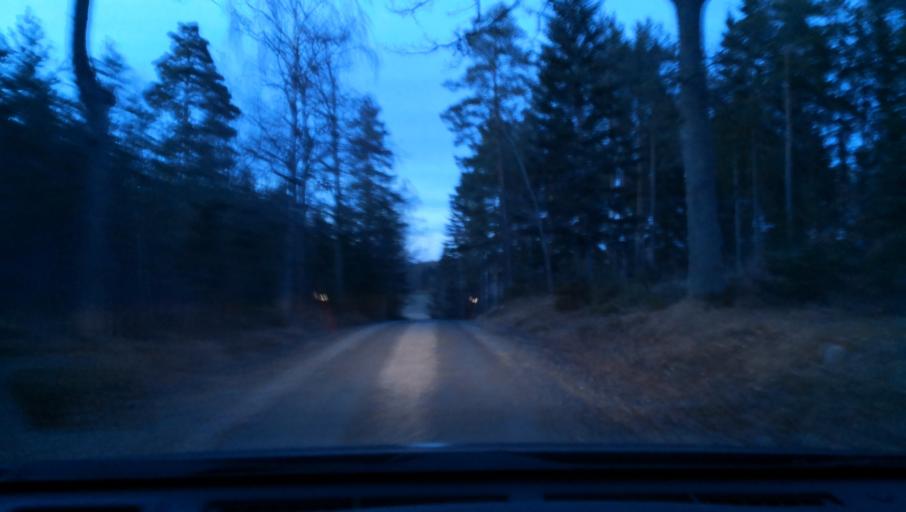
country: SE
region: Uppsala
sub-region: Enkopings Kommun
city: Dalby
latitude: 59.5647
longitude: 17.3738
